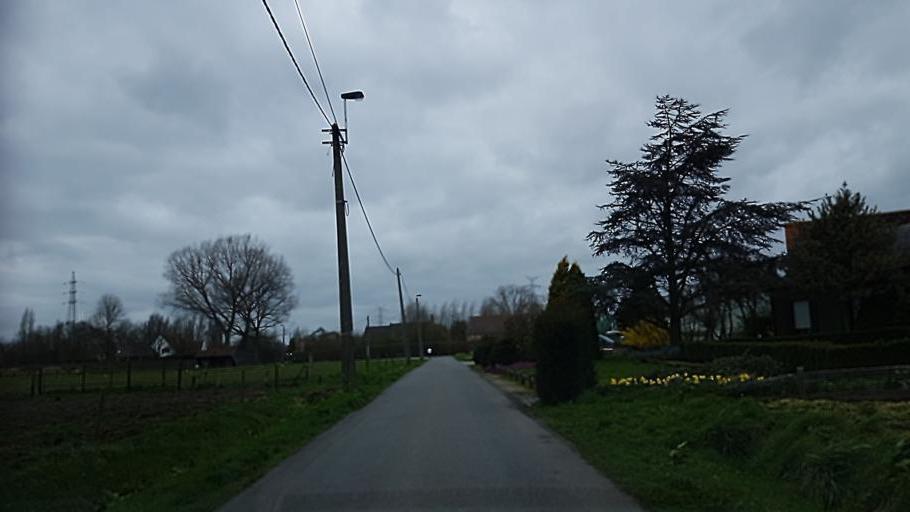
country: BE
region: Flanders
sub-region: Provincie Antwerpen
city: Duffel
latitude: 51.1106
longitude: 4.5117
